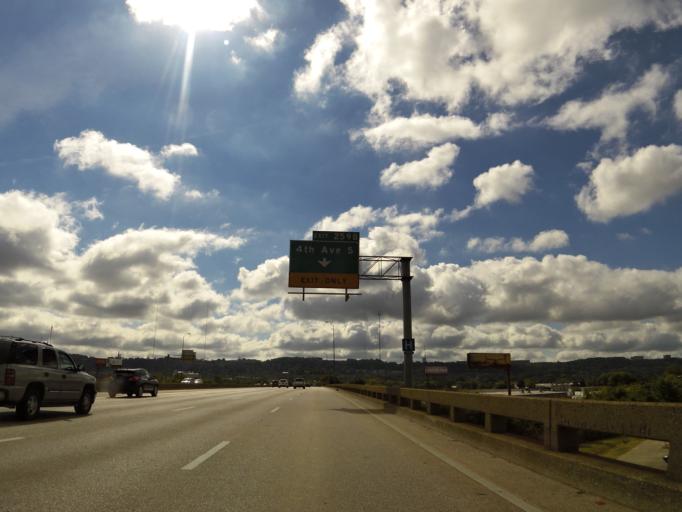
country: US
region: Alabama
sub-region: Jefferson County
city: Birmingham
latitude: 33.5065
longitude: -86.8179
